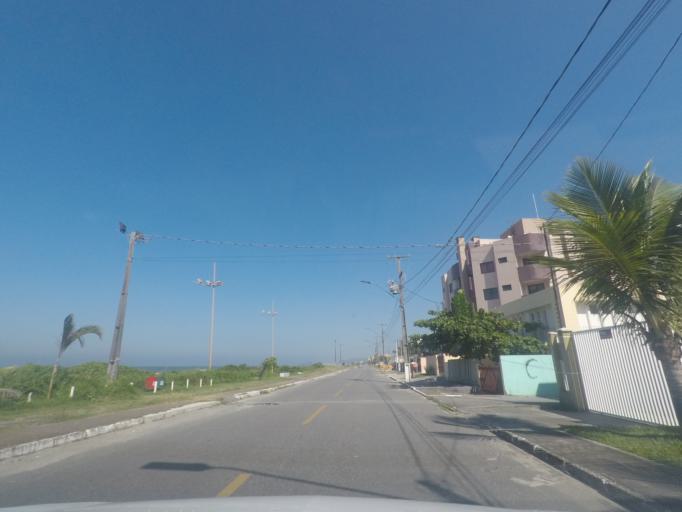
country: BR
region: Parana
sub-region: Pontal Do Parana
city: Pontal do Parana
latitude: -25.7565
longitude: -48.5041
